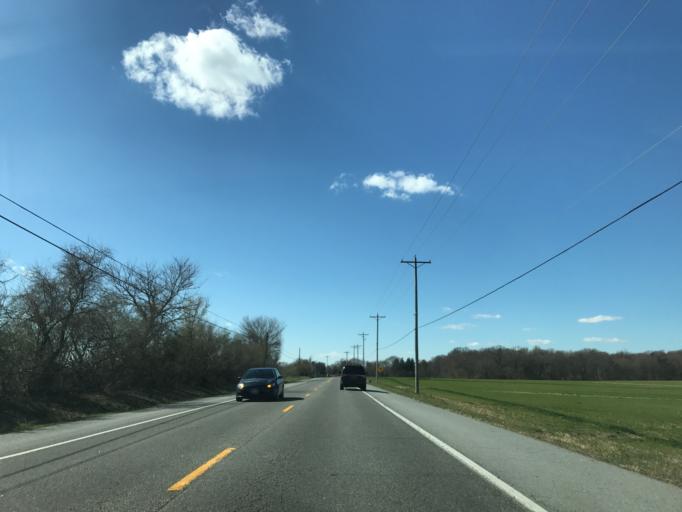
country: US
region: Maryland
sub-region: Kent County
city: Chestertown
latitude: 39.2214
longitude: -76.1559
